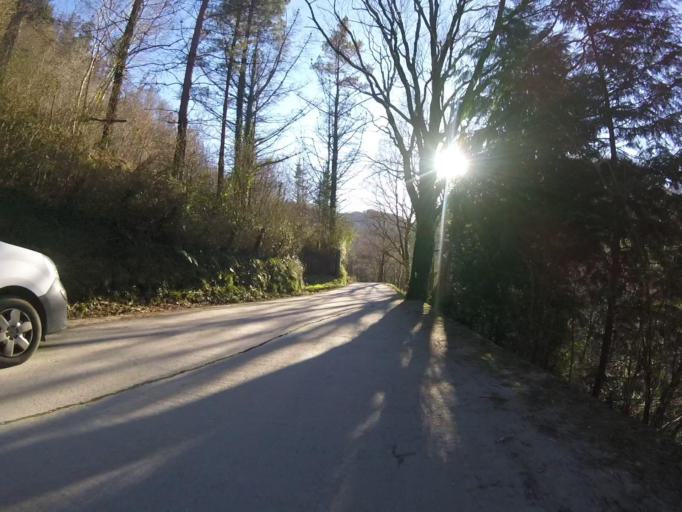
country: ES
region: Basque Country
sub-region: Provincia de Guipuzcoa
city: Errenteria
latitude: 43.2837
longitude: -1.8704
